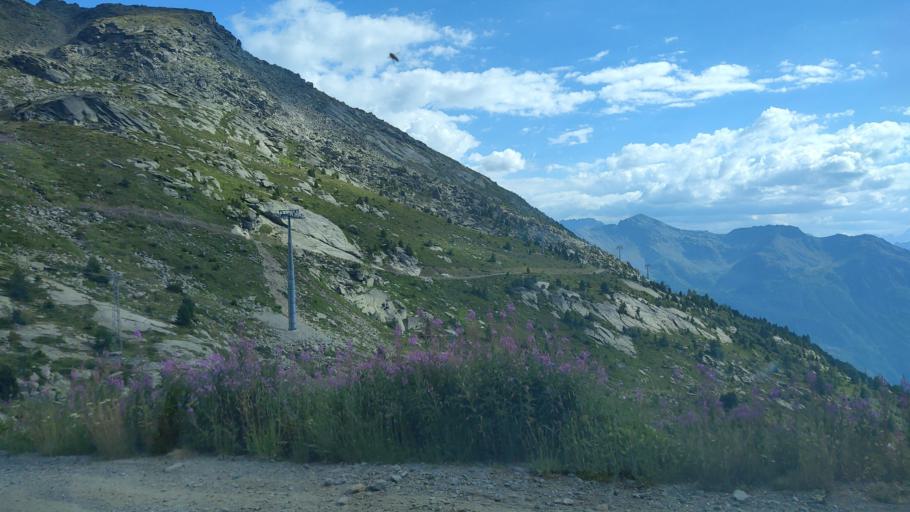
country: FR
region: Rhone-Alpes
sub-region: Departement de la Savoie
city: Val Thorens
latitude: 45.2446
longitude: 6.5672
